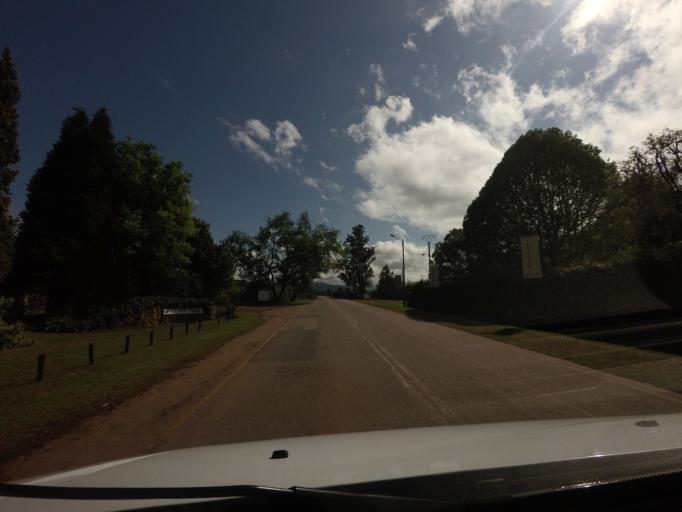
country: ZA
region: Mpumalanga
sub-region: Ehlanzeni District
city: Graksop
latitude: -25.0929
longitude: 30.7730
